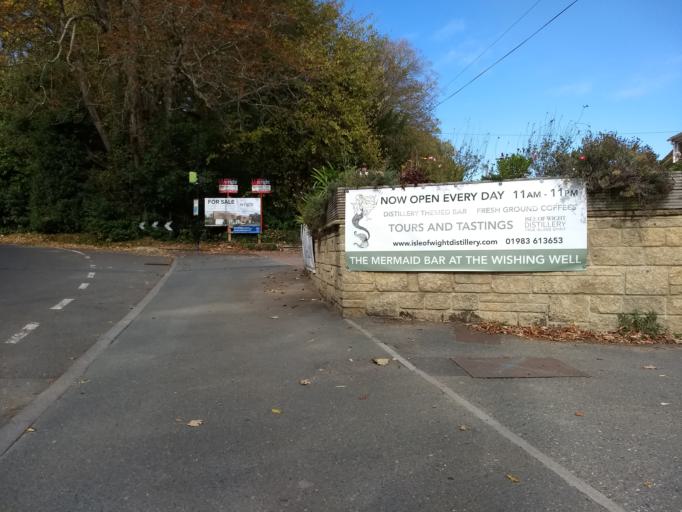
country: GB
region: England
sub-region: Isle of Wight
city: Seaview
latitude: 50.7166
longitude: -1.1245
